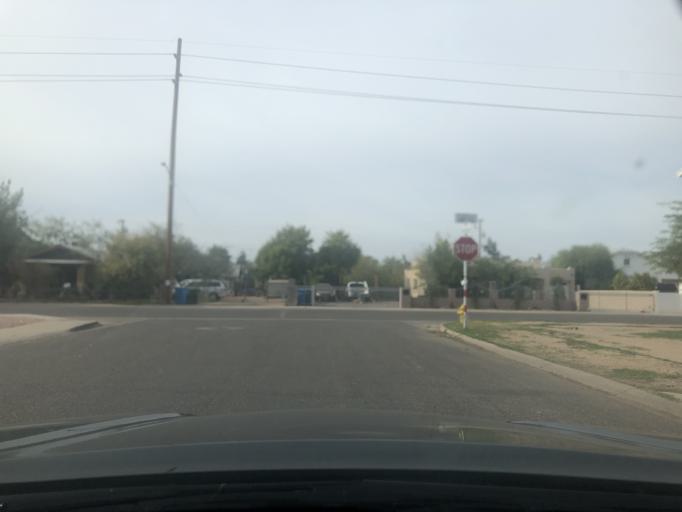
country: US
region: Arizona
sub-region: Maricopa County
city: Phoenix
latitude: 33.4595
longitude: -112.0430
